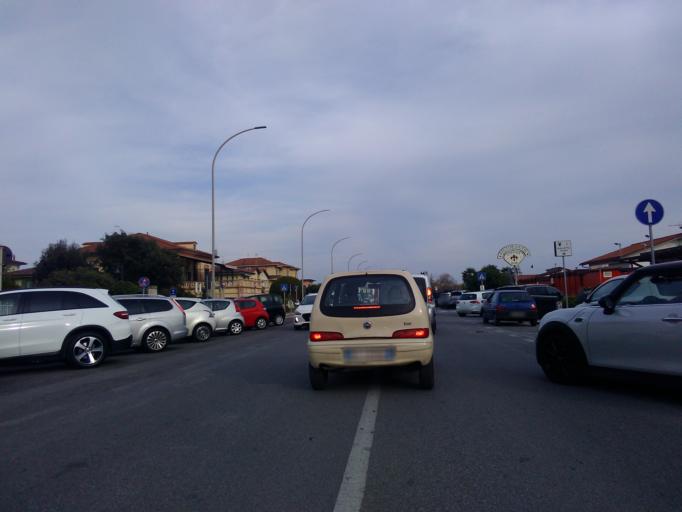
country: IT
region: Tuscany
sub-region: Provincia di Massa-Carrara
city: Massa
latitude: 44.0058
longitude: 10.1022
